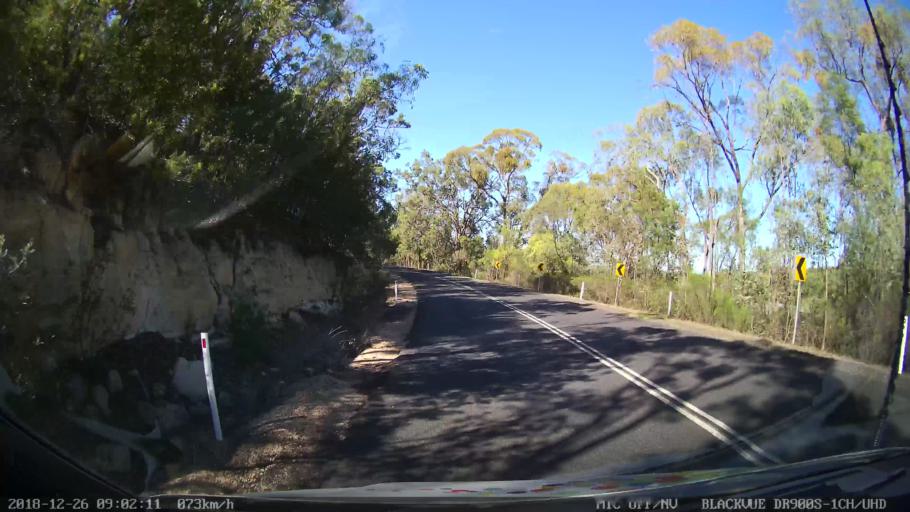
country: AU
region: New South Wales
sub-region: Mid-Western Regional
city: Kandos
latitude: -32.6502
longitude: 150.0202
